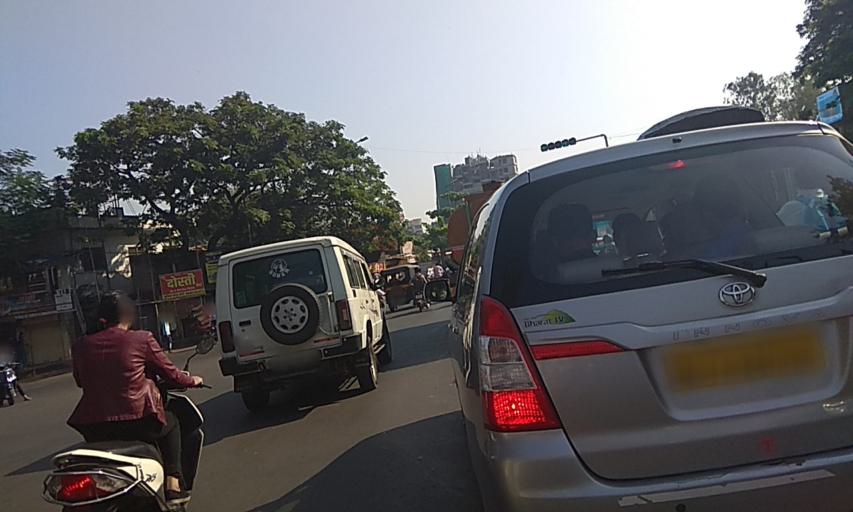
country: IN
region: Maharashtra
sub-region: Pune Division
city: Pune
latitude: 18.5012
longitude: 73.8456
